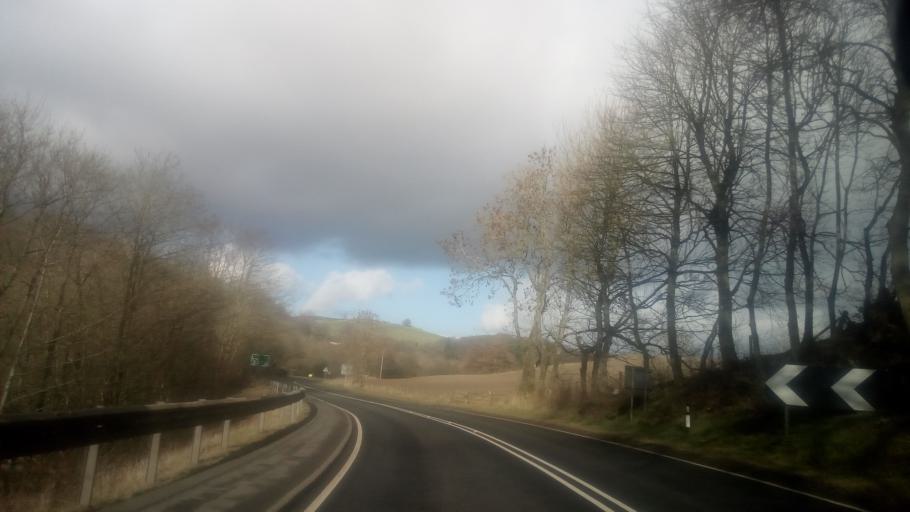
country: GB
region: Scotland
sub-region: The Scottish Borders
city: Hawick
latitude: 55.4121
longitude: -2.8198
